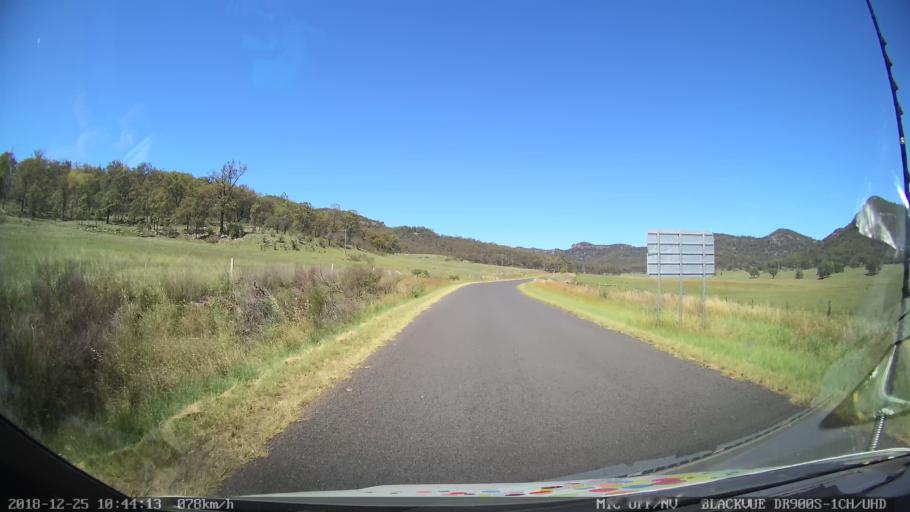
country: AU
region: New South Wales
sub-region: Upper Hunter Shire
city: Merriwa
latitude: -32.4272
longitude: 150.3034
